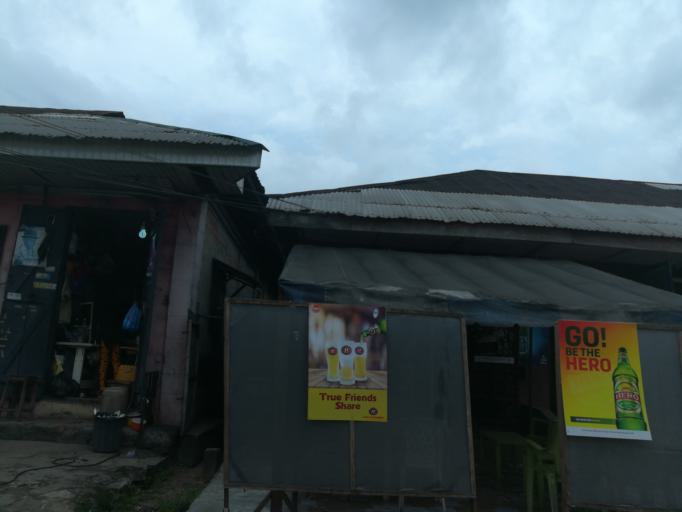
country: NG
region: Rivers
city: Port Harcourt
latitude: 4.7608
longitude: 7.0192
